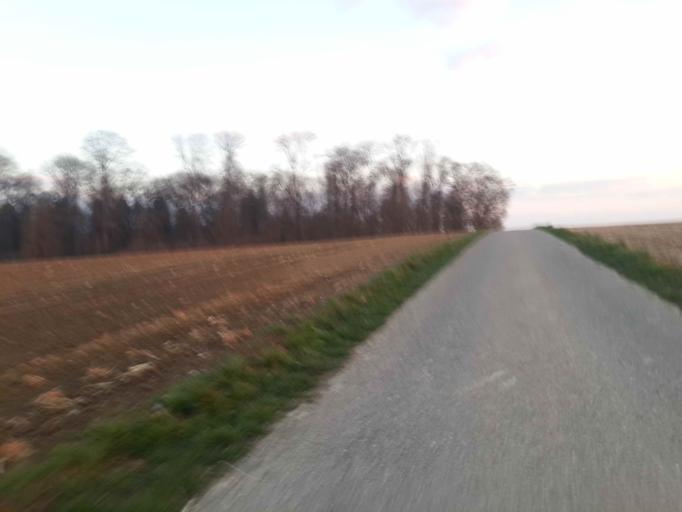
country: DE
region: Baden-Wuerttemberg
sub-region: Regierungsbezirk Stuttgart
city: Bad Rappenau
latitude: 49.2321
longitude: 9.0719
